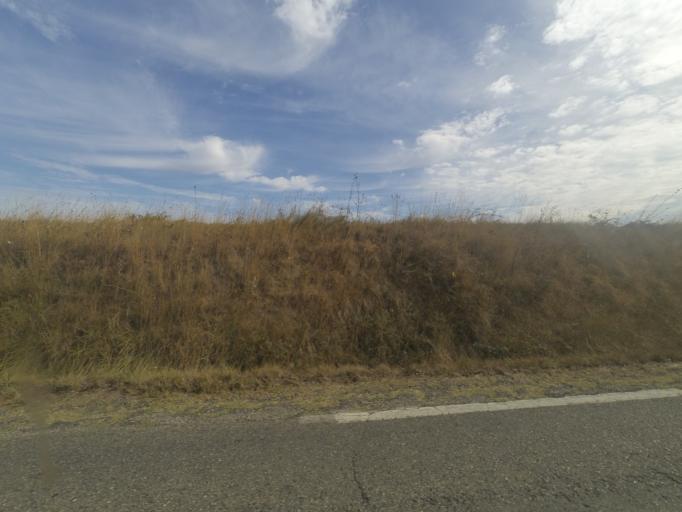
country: FR
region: Languedoc-Roussillon
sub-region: Departement du Gard
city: Nages-et-Solorgues
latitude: 43.7855
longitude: 4.2137
